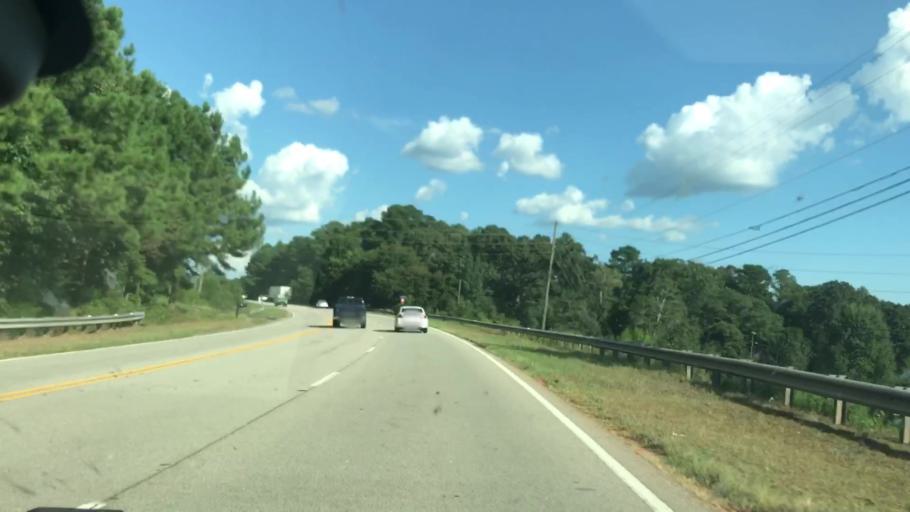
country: US
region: Georgia
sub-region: Troup County
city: La Grange
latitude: 32.9631
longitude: -84.9817
